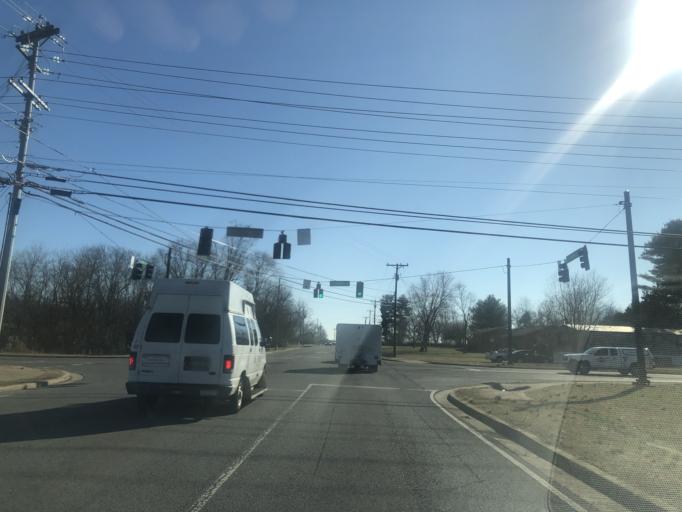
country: US
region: Tennessee
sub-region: Rutherford County
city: Smyrna
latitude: 35.9139
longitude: -86.4702
